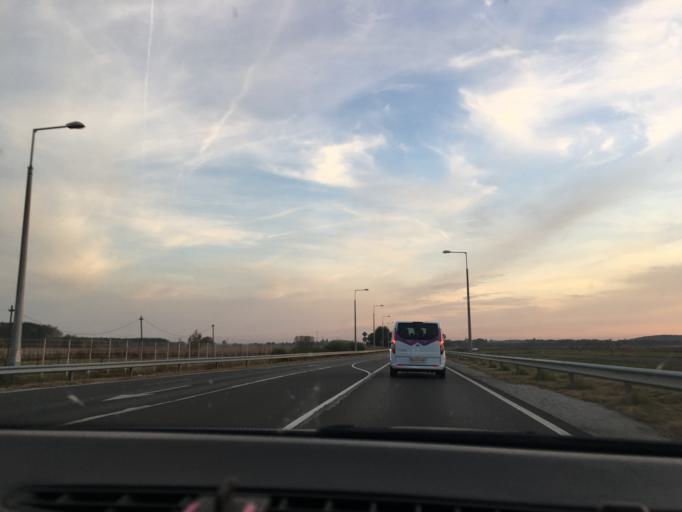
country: HU
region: Hajdu-Bihar
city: Teglas
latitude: 47.7088
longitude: 21.6592
